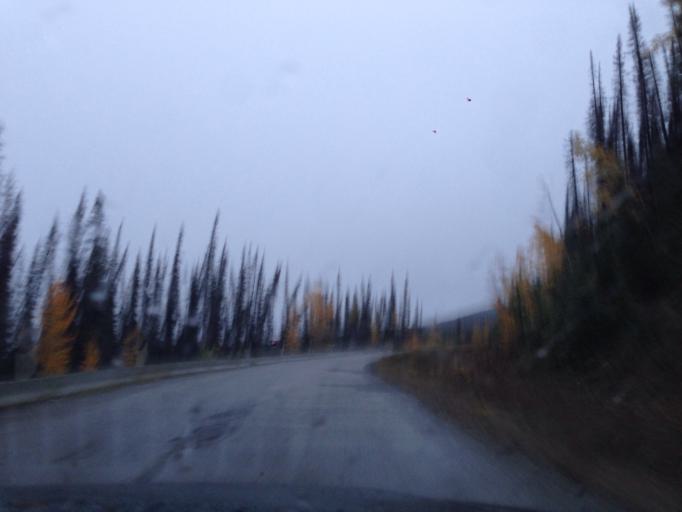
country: CA
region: Yukon
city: Watson Lake
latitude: 59.6857
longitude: -129.1522
